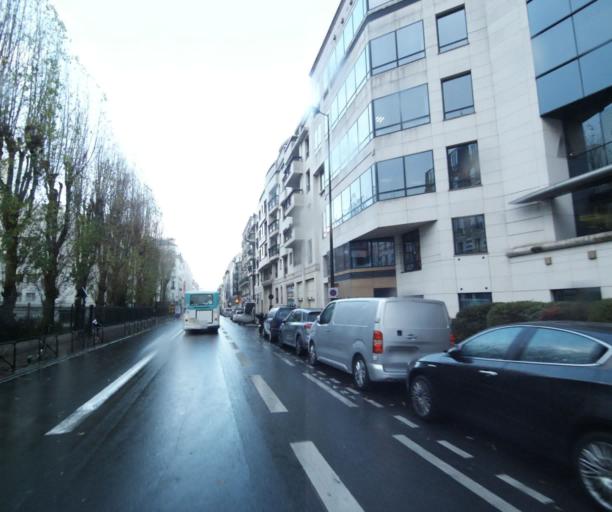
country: FR
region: Ile-de-France
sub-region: Departement des Hauts-de-Seine
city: Levallois-Perret
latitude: 48.8970
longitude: 2.2958
